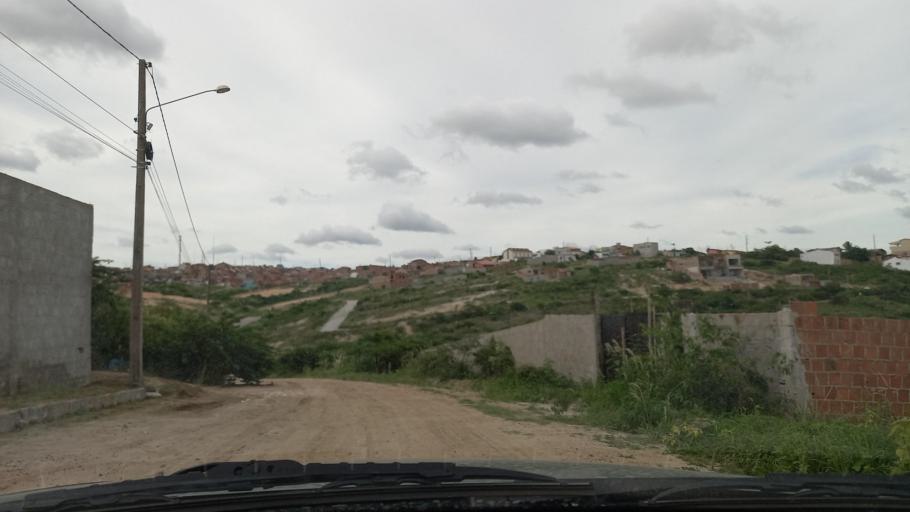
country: BR
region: Pernambuco
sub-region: Gravata
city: Gravata
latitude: -8.2205
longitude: -35.5754
